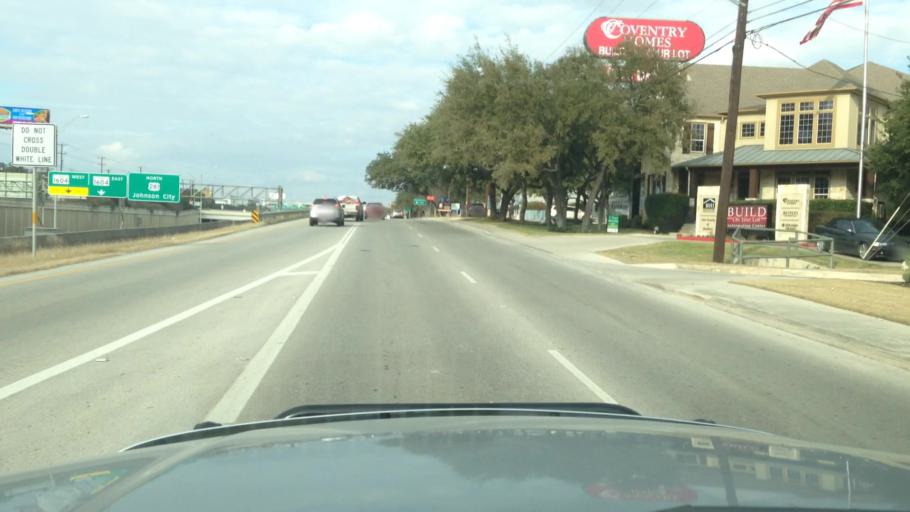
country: US
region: Texas
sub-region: Bexar County
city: Hollywood Park
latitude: 29.5957
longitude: -98.4719
